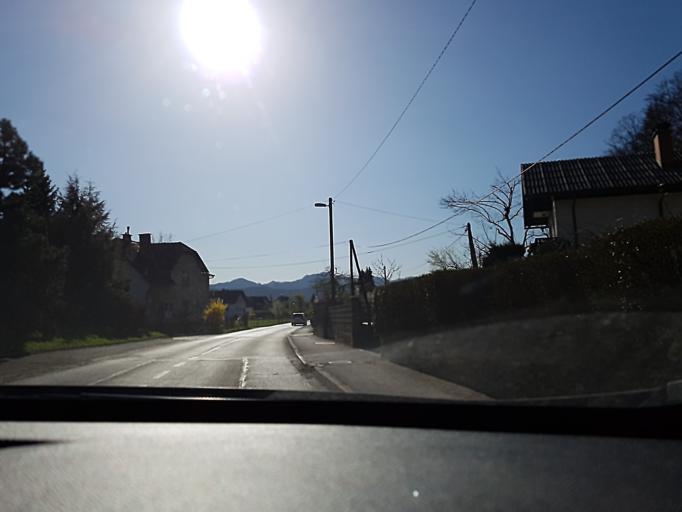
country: SI
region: Medvode
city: Zgornje Pirnice
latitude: 46.1212
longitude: 14.4731
